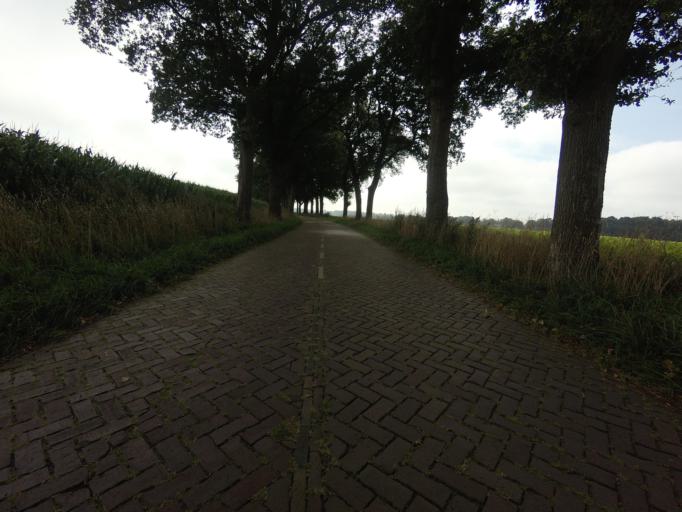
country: NL
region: Drenthe
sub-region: Gemeente Tynaarlo
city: Vries
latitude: 53.1065
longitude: 6.5373
